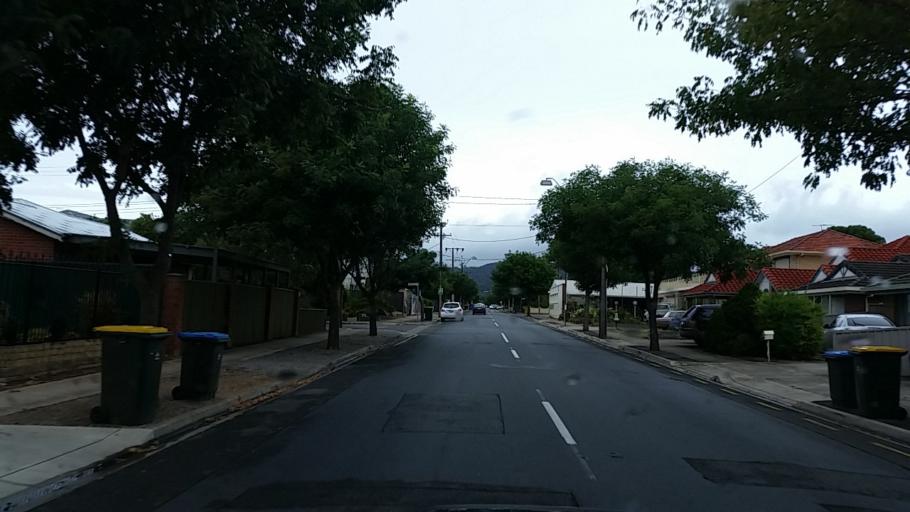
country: AU
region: South Australia
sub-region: Campbelltown
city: Hectorville
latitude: -34.8972
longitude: 138.6631
